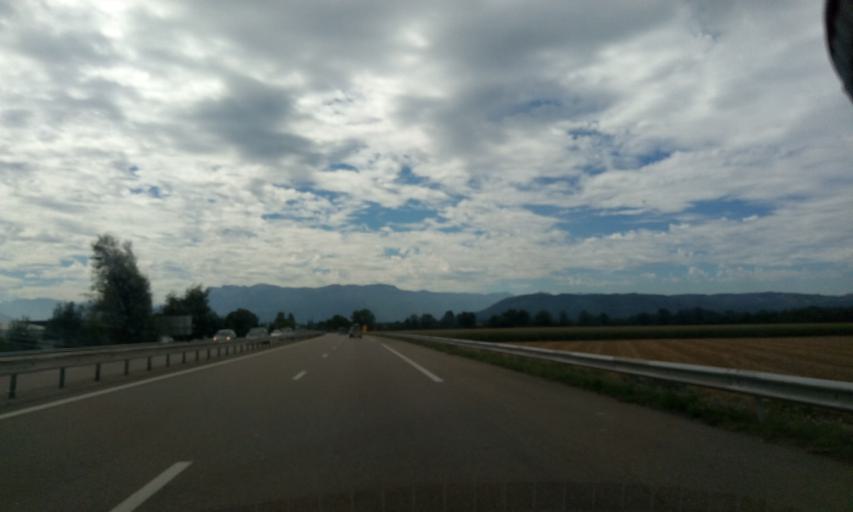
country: FR
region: Rhone-Alpes
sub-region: Departement de l'Isere
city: Colombe
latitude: 45.3964
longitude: 5.4662
